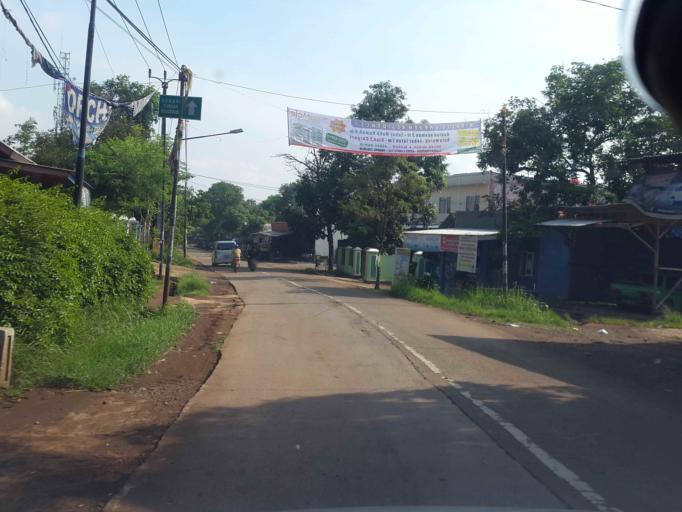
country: ID
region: West Java
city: Cileungsir
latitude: -6.3471
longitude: 107.0347
